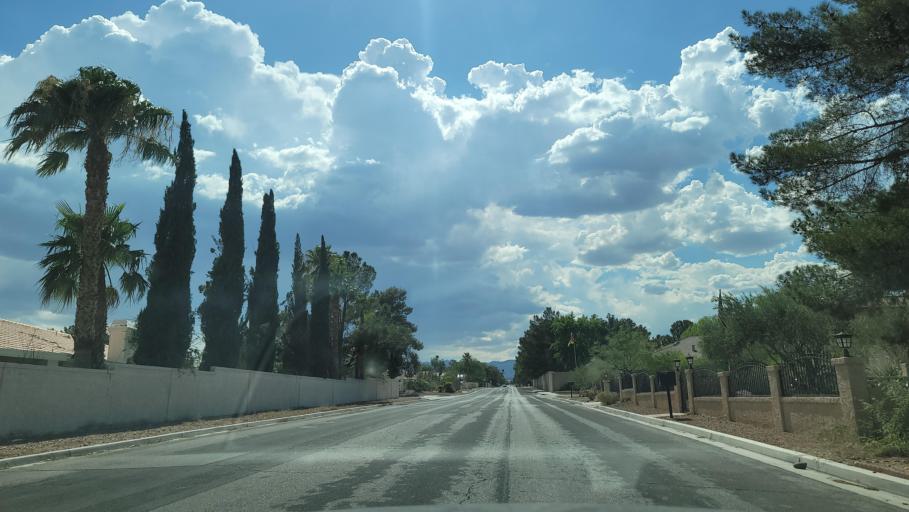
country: US
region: Nevada
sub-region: Clark County
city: Spring Valley
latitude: 36.1312
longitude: -115.2488
